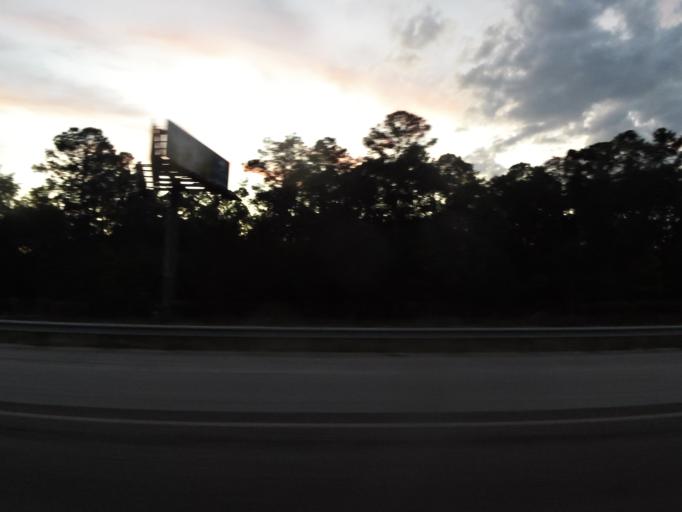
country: US
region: Georgia
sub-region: Liberty County
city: Midway
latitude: 31.8156
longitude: -81.3627
